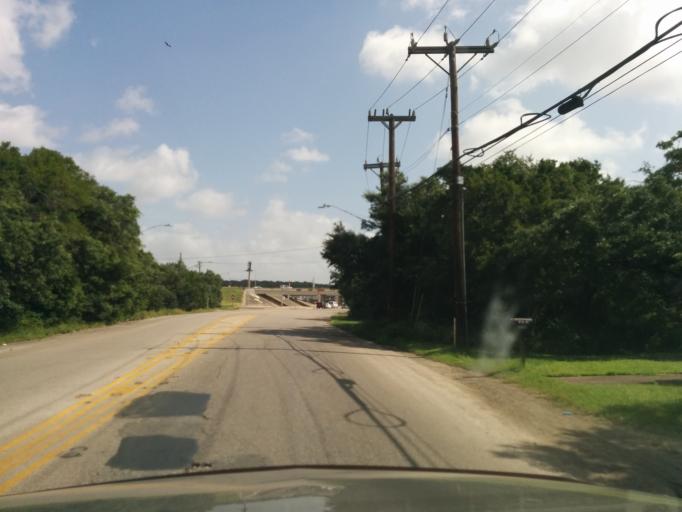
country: US
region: Texas
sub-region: Bexar County
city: Helotes
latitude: 29.5847
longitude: -98.6315
